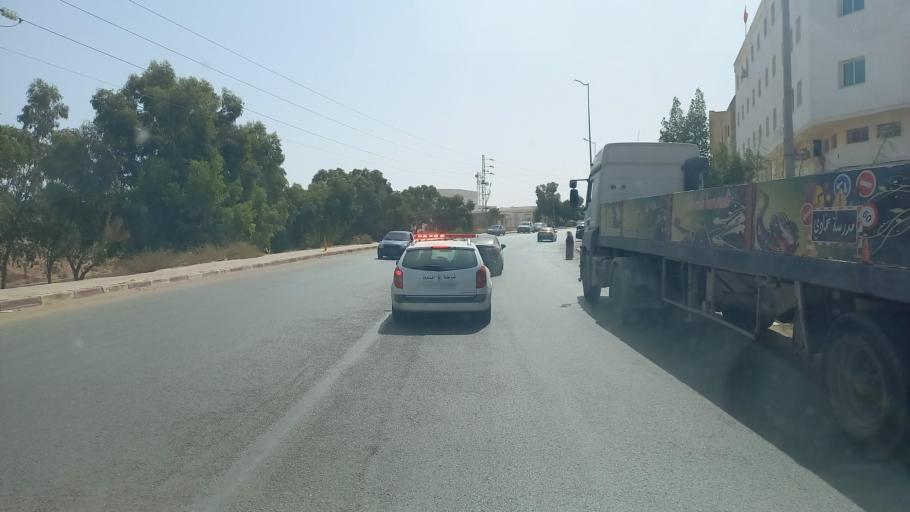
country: TN
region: Madanin
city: Medenine
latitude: 33.3444
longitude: 10.5012
